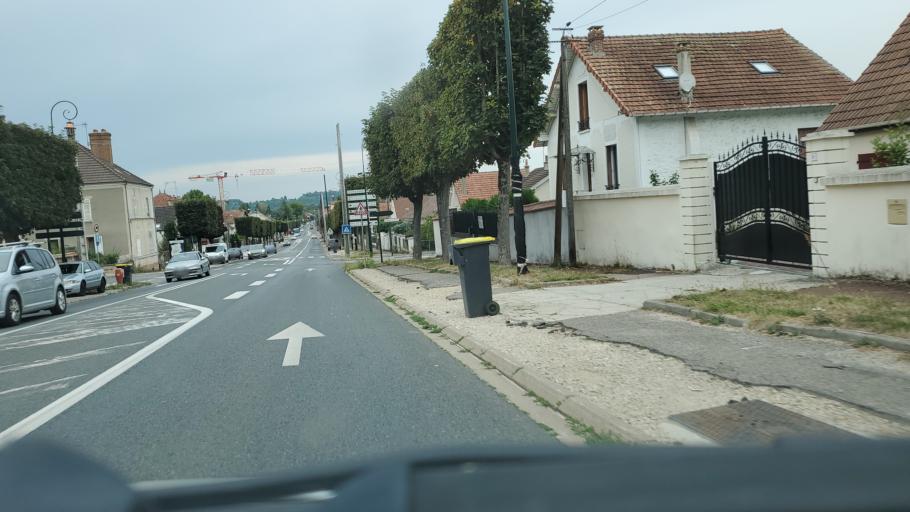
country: FR
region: Ile-de-France
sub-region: Departement de Seine-et-Marne
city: Coulommiers
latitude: 48.8009
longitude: 3.0869
